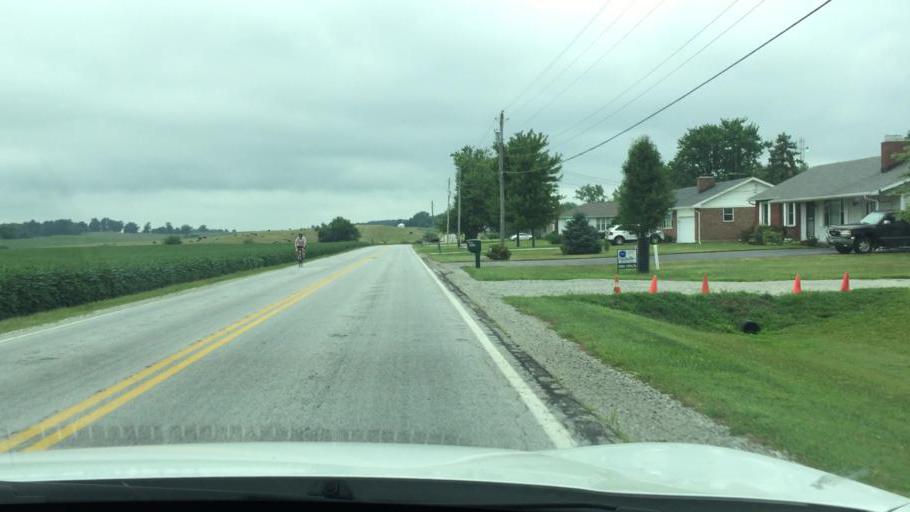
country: US
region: Ohio
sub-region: Clark County
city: Lisbon
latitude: 39.9438
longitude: -83.6819
